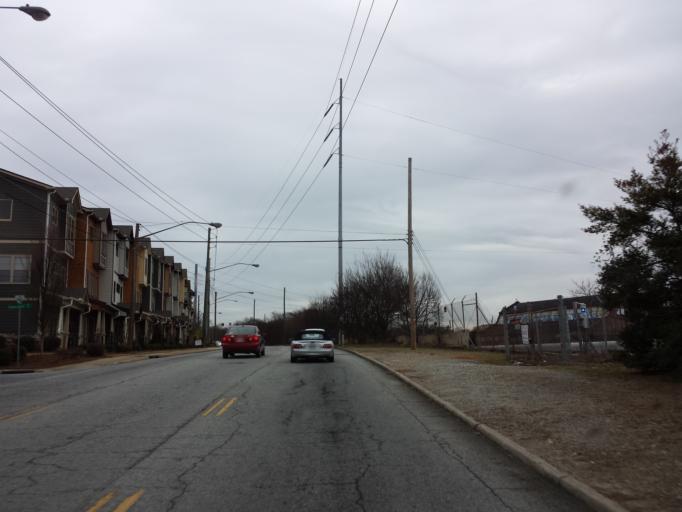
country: US
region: Georgia
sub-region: DeKalb County
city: Druid Hills
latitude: 33.7609
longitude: -84.3296
